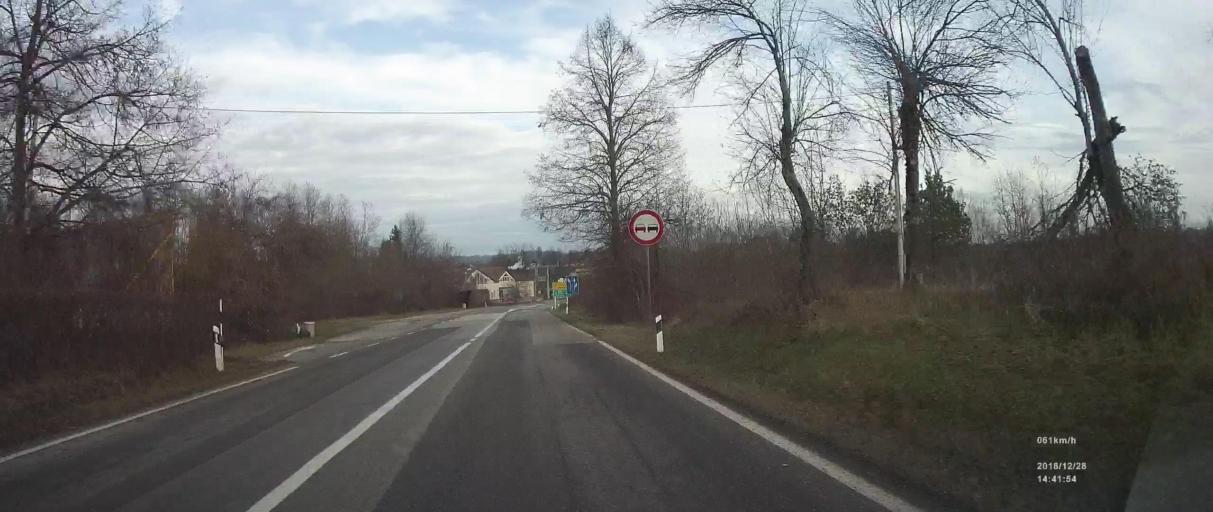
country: SI
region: Crnomelj
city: Crnomelj
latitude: 45.4410
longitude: 15.2605
